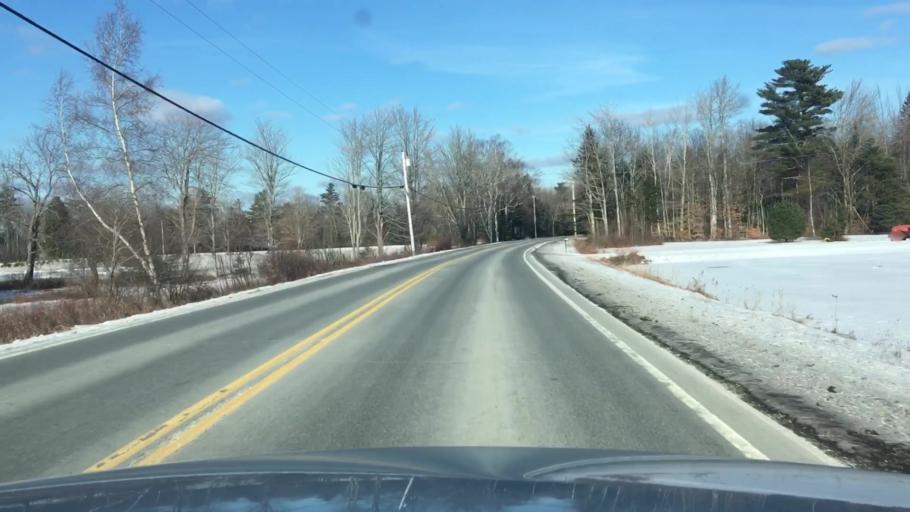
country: US
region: Maine
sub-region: Penobscot County
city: Holden
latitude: 44.7654
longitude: -68.5941
